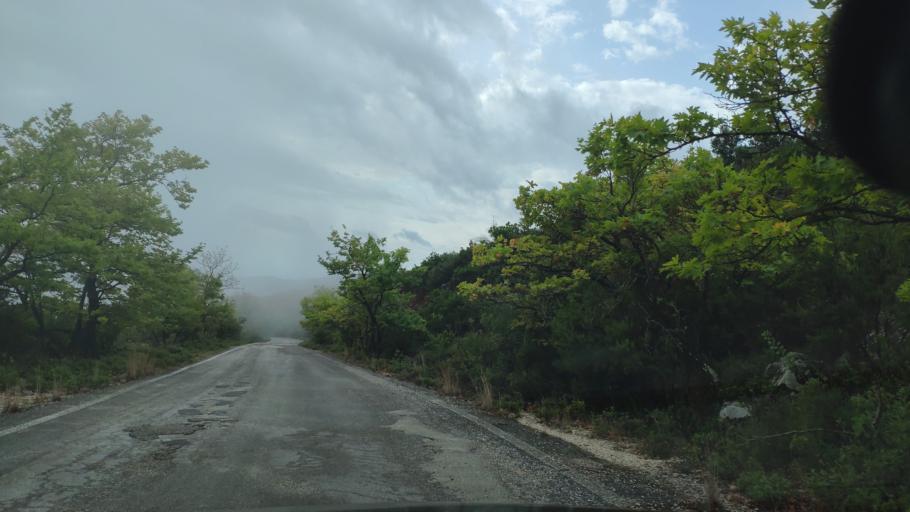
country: GR
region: West Greece
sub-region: Nomos Aitolias kai Akarnanias
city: Sardinia
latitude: 38.8491
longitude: 21.3156
